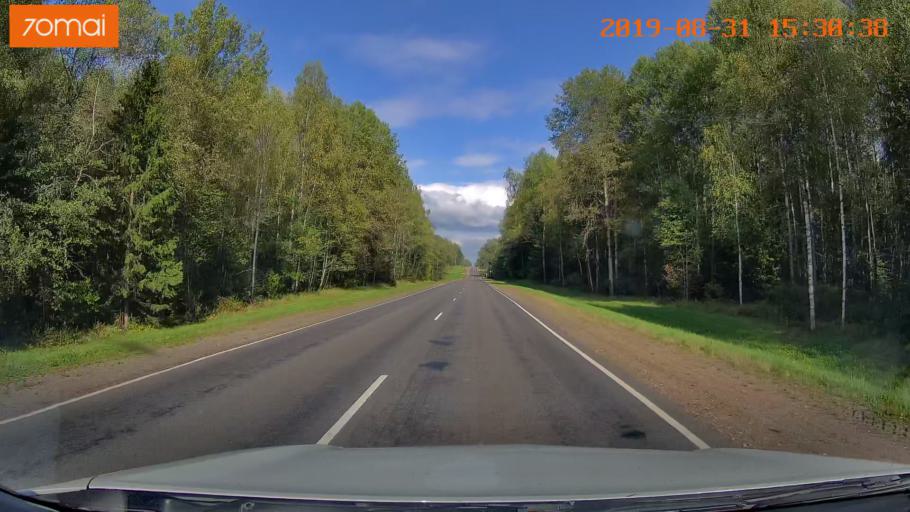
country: RU
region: Kaluga
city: Baryatino
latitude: 54.5770
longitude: 34.6350
